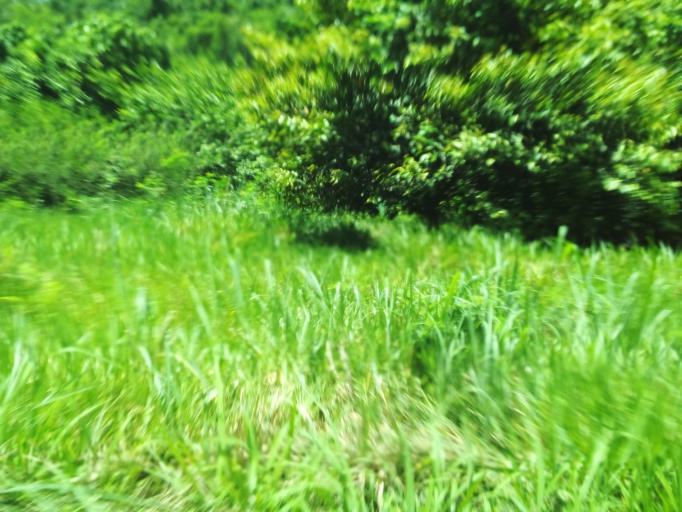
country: BR
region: Espirito Santo
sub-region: Serra
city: Serra
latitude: -20.1267
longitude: -40.4141
